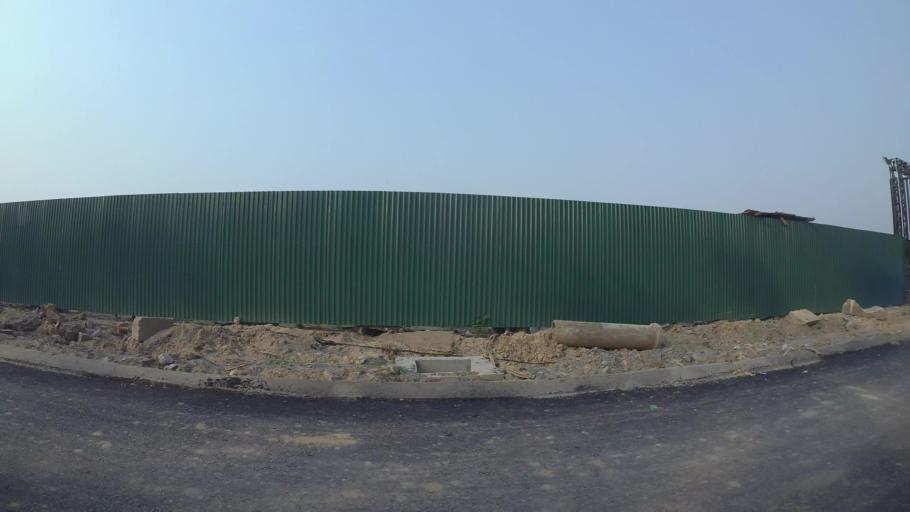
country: VN
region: Ha Noi
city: Tay Ho
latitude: 21.0761
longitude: 105.8081
